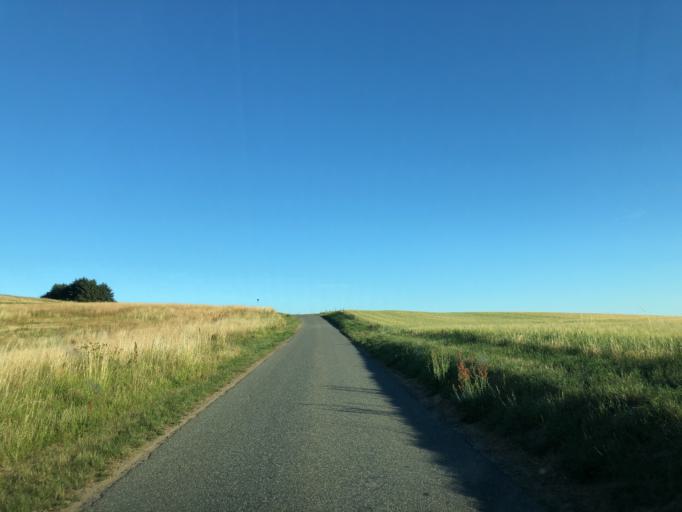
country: DK
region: Central Jutland
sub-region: Skanderborg Kommune
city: Ry
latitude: 55.9841
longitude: 9.7935
